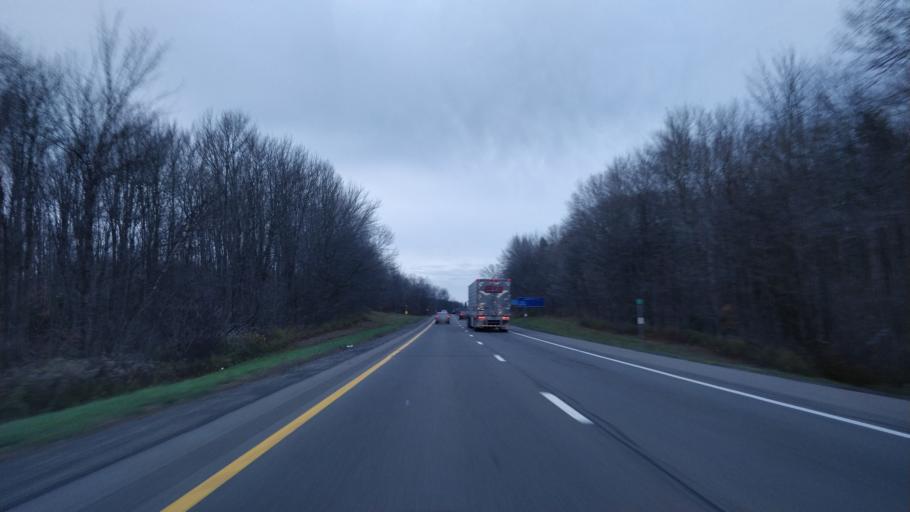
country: US
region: New York
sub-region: Oswego County
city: Central Square
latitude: 43.3958
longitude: -76.1184
